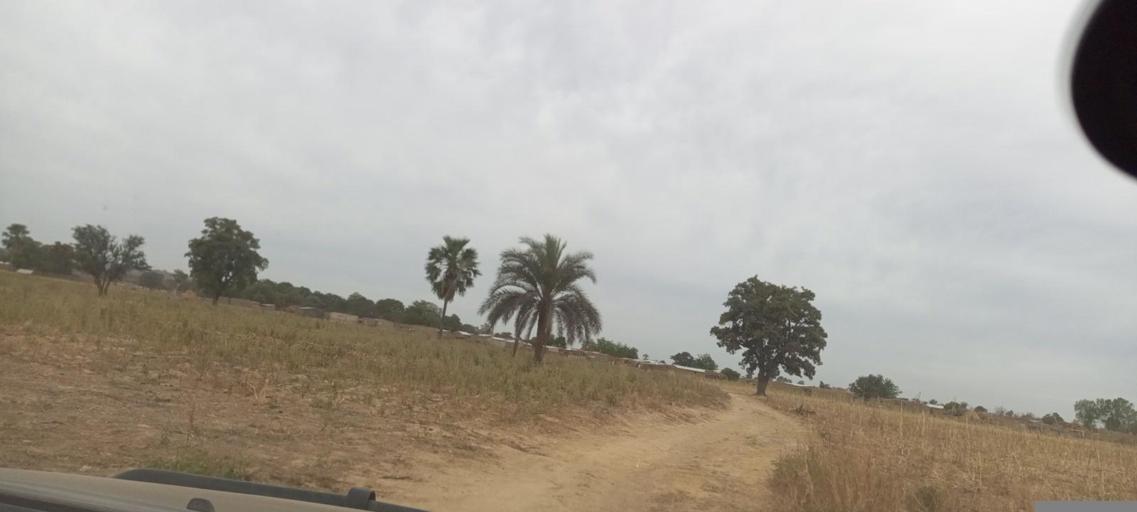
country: ML
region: Koulikoro
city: Kati
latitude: 12.7468
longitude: -8.3577
